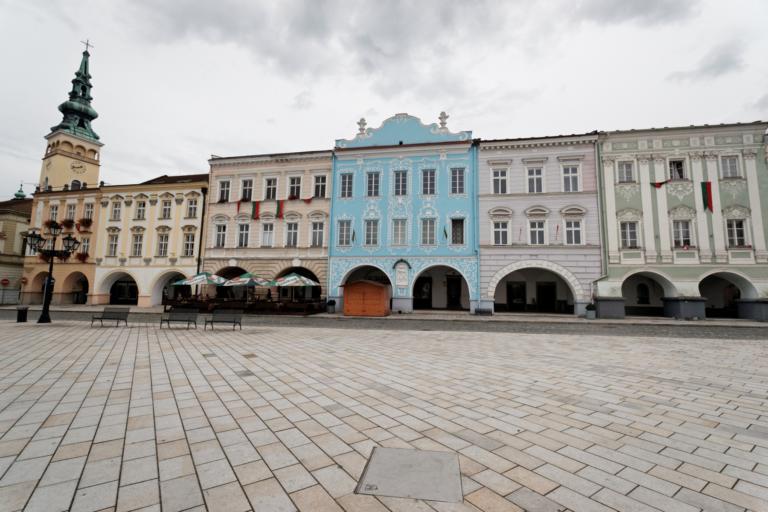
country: CZ
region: Moravskoslezsky
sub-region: Okres Novy Jicin
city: Novy Jicin
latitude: 49.5947
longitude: 18.0108
